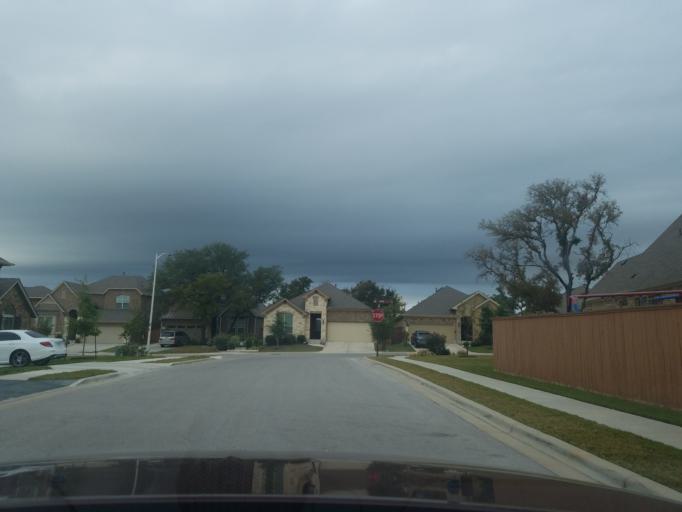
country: US
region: Texas
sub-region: Williamson County
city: Cedar Park
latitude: 30.4880
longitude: -97.7904
